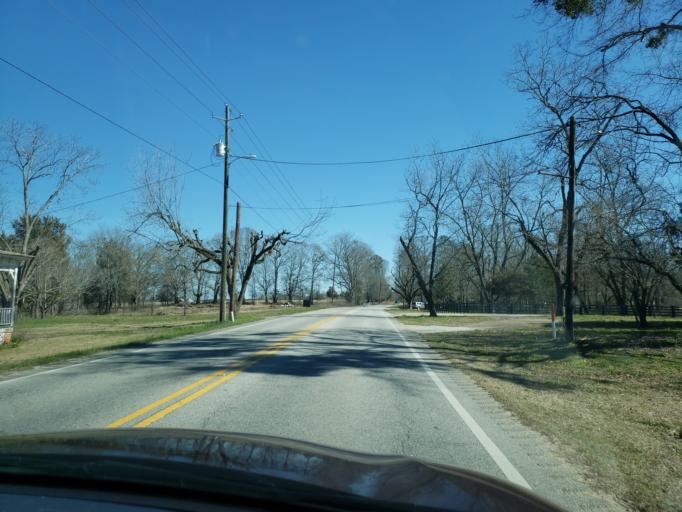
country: US
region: Alabama
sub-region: Lee County
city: Auburn
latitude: 32.6043
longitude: -85.5915
